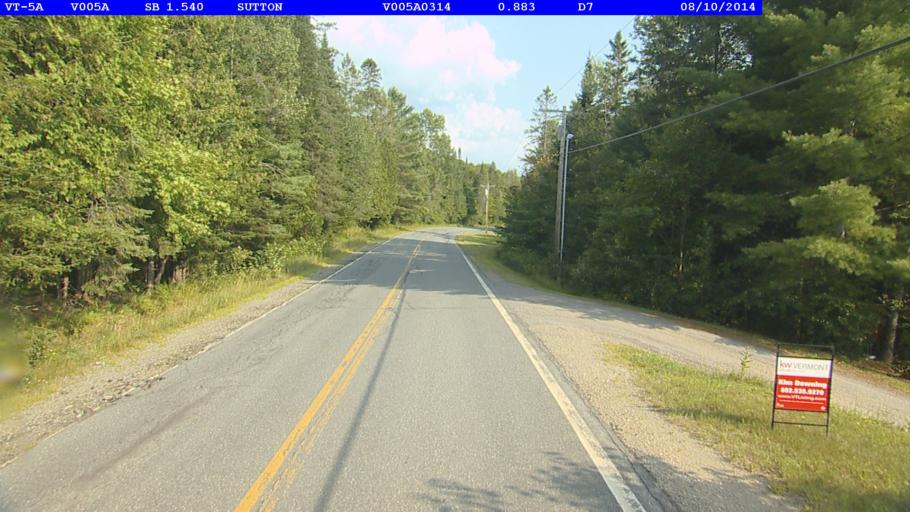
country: US
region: Vermont
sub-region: Caledonia County
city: Lyndonville
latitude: 44.6606
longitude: -71.9900
